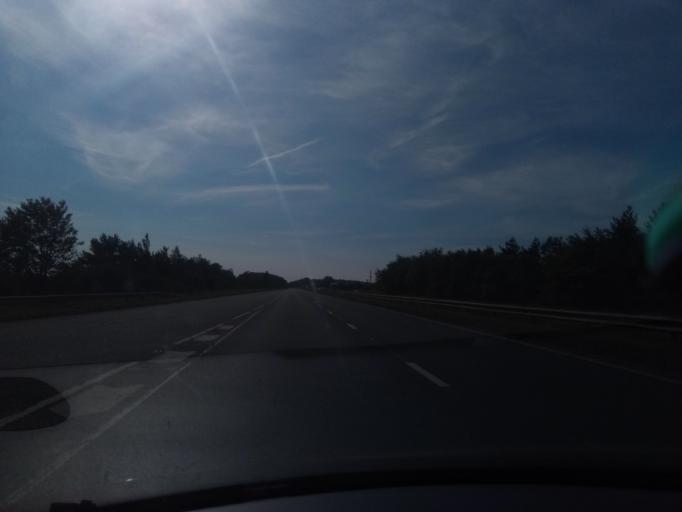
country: GB
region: England
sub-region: County Durham
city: Seaham
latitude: 54.8359
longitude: -1.3751
